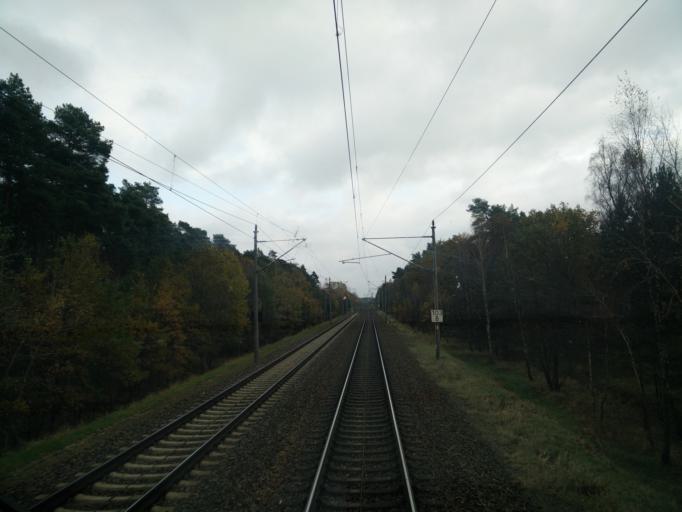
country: DE
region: Brandenburg
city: Plattenburg
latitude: 52.9130
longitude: 12.0588
